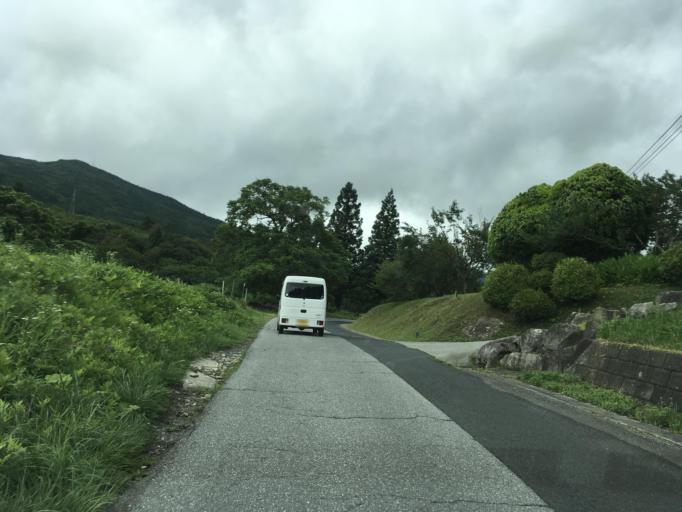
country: JP
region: Iwate
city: Ofunato
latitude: 38.8898
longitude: 141.4810
